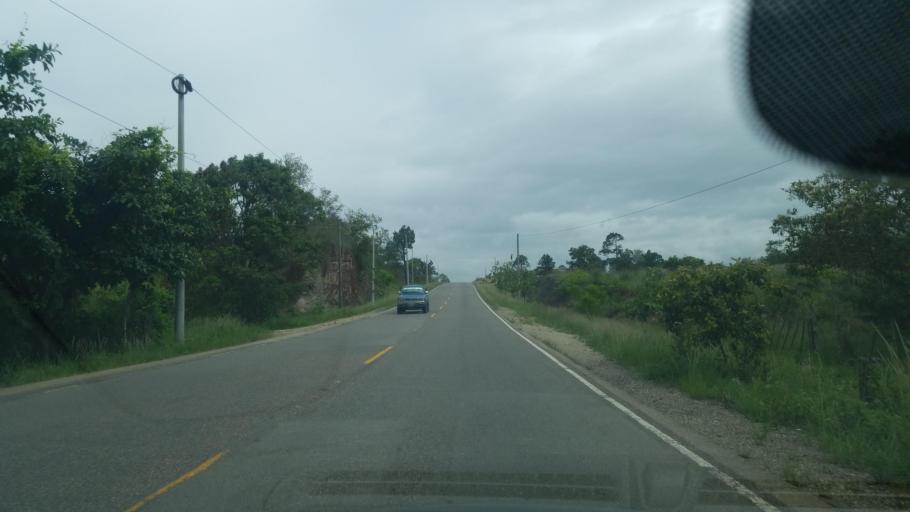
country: HN
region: Ocotepeque
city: Lucerna
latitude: 14.5748
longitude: -88.9299
